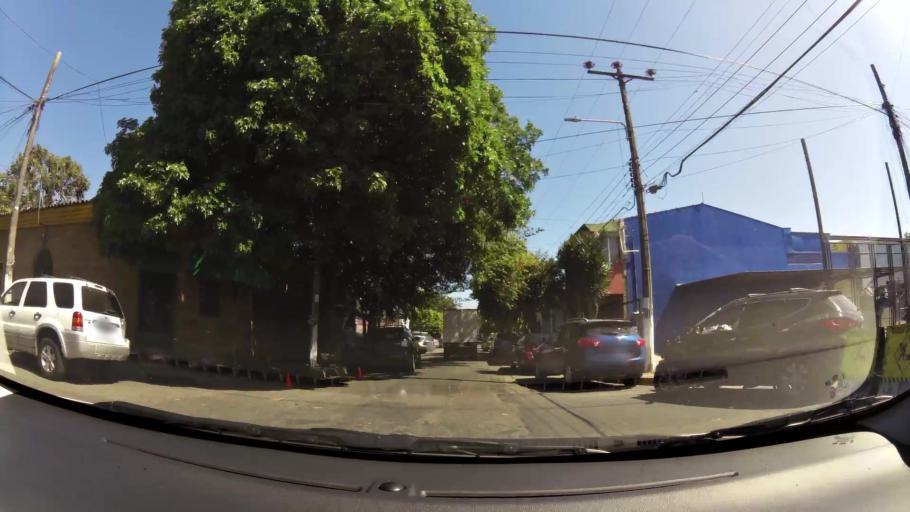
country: SV
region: La Libertad
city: Santa Tecla
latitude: 13.6745
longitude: -89.2925
